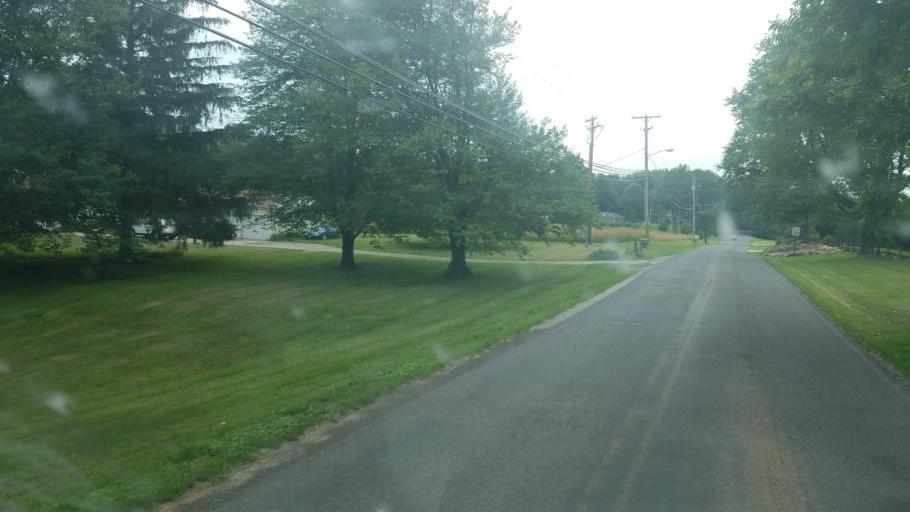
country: US
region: Ohio
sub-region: Summit County
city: Clinton
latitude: 40.9297
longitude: -81.6197
